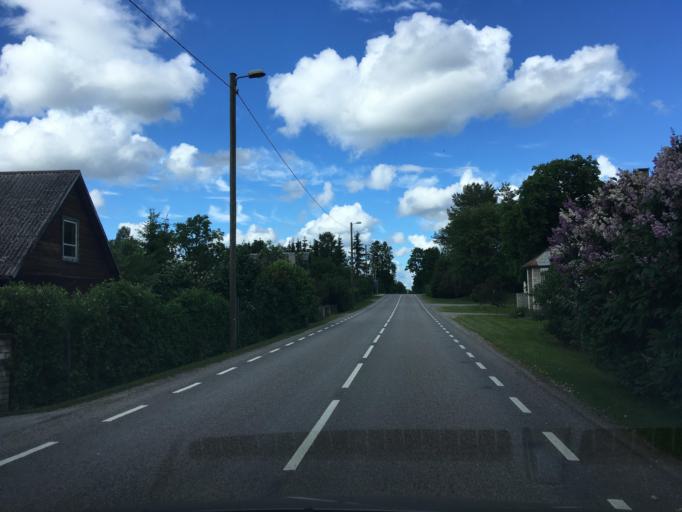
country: EE
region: Paernumaa
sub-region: Tootsi vald
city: Tootsi
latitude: 58.6681
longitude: 24.7554
